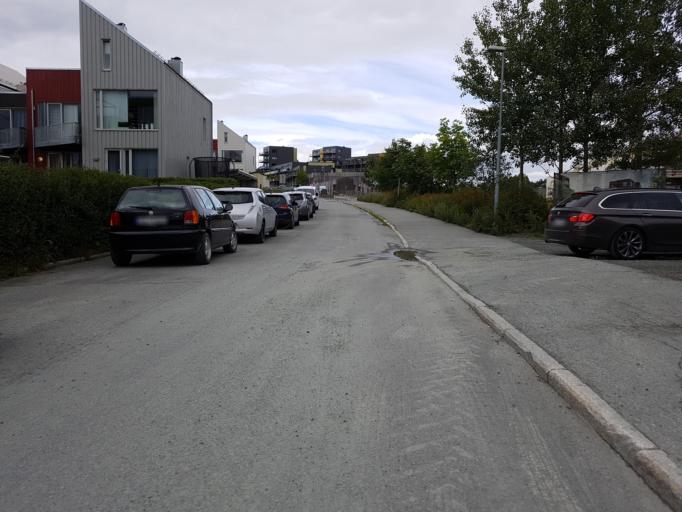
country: NO
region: Sor-Trondelag
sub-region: Trondheim
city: Trondheim
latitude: 63.3885
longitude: 10.4348
